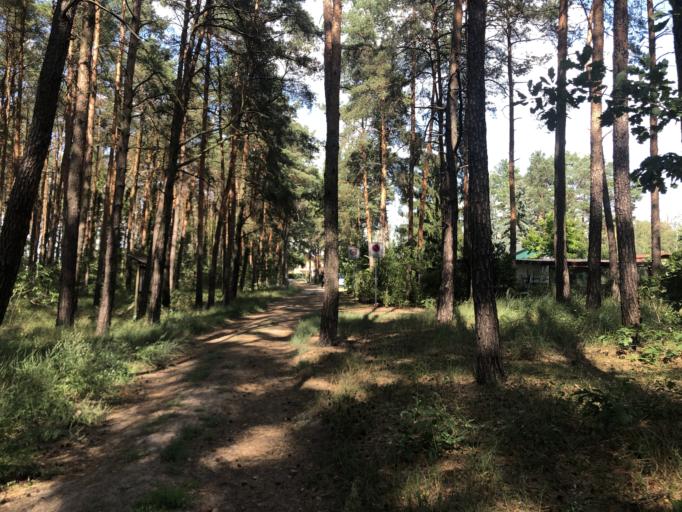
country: DE
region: Brandenburg
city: Mullrose
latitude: 52.2343
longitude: 14.4057
